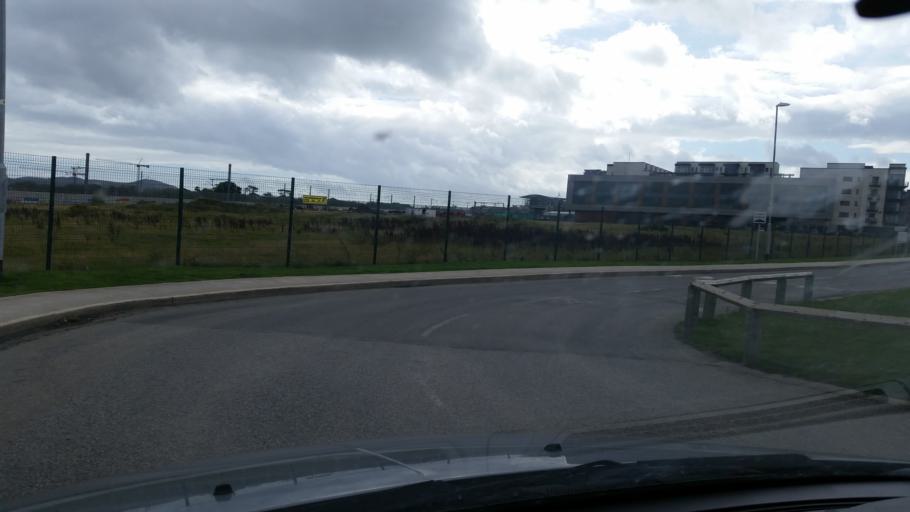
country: IE
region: Leinster
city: Donaghmede
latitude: 53.4064
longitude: -6.1512
